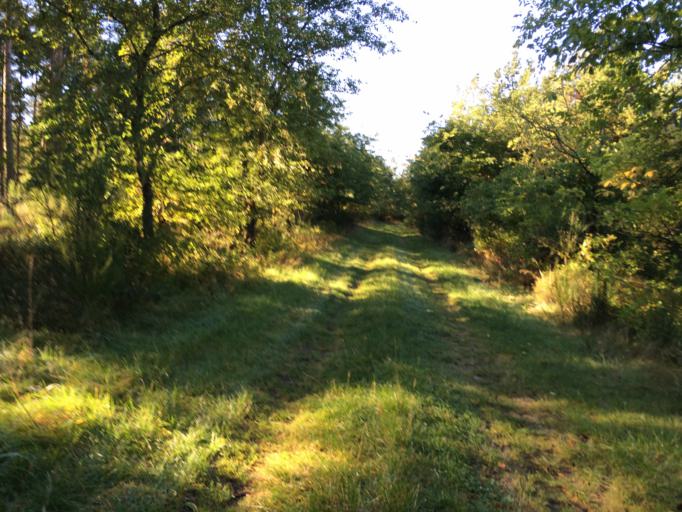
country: DK
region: Central Jutland
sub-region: Holstebro Kommune
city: Ulfborg
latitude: 56.2451
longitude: 8.3674
